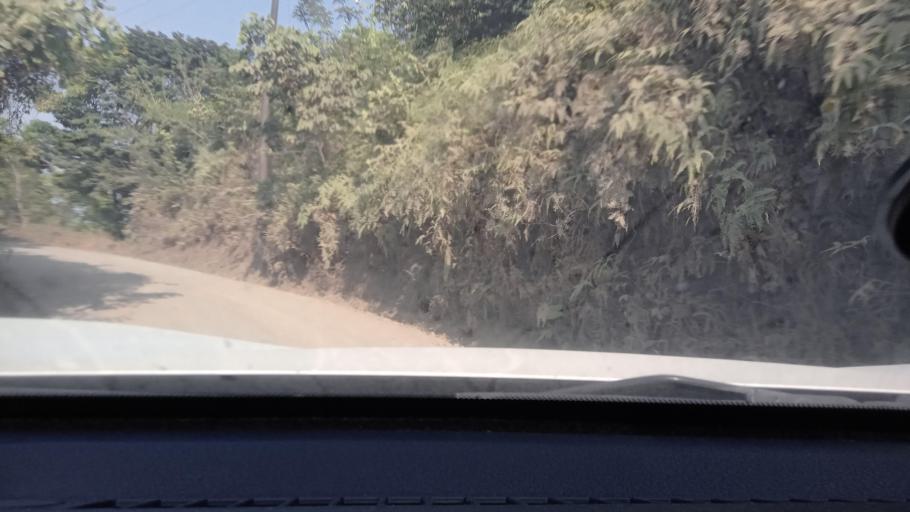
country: MX
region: Tabasco
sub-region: Huimanguillo
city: Francisco Rueda
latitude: 17.6528
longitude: -93.8828
